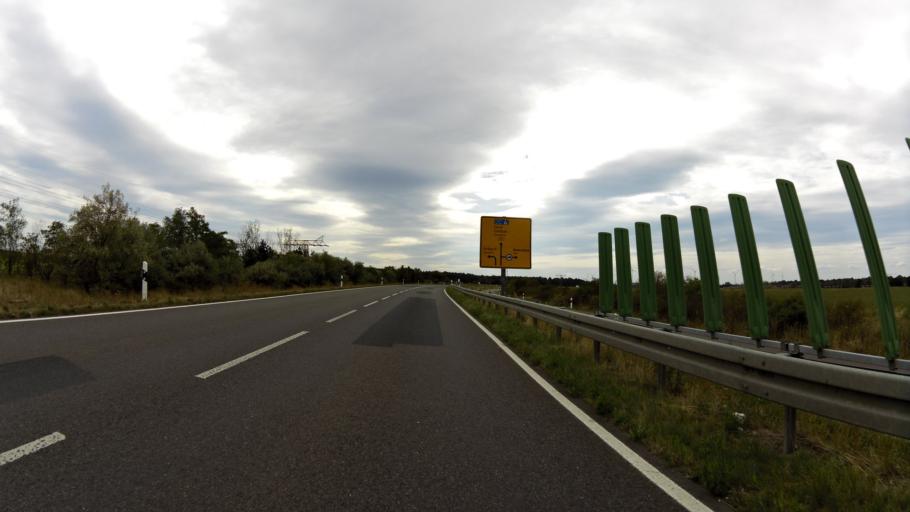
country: DE
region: Brandenburg
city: Heinersbruck
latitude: 51.8102
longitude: 14.5055
